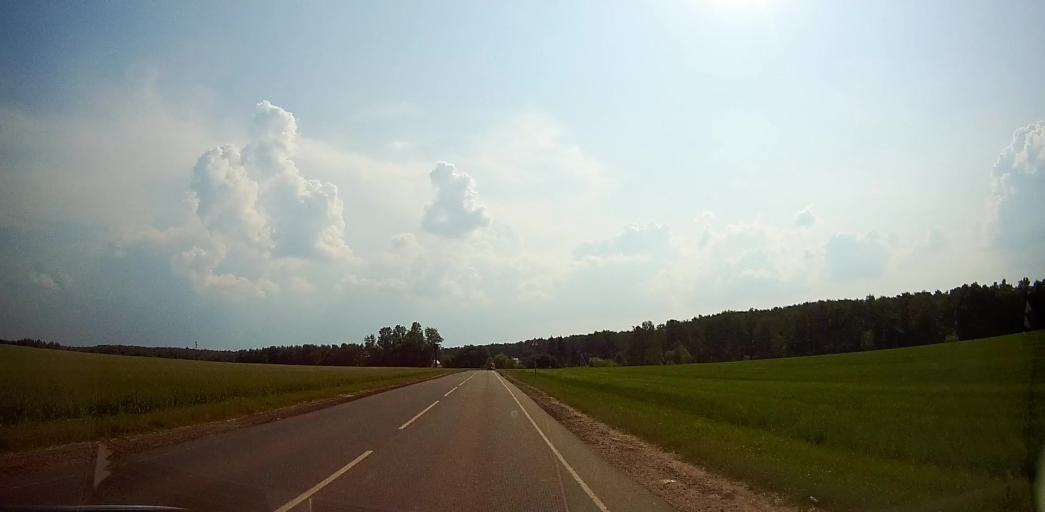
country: RU
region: Moskovskaya
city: Il'inskoye
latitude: 55.2869
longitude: 37.9381
